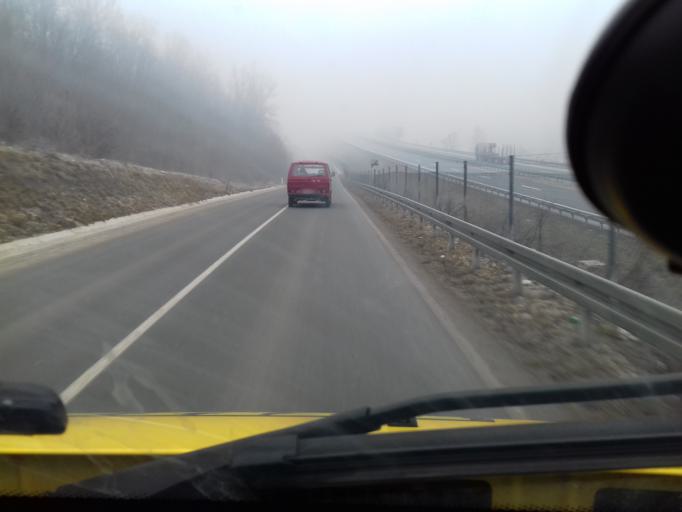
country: BA
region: Federation of Bosnia and Herzegovina
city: Kakanj
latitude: 44.1307
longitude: 18.0869
